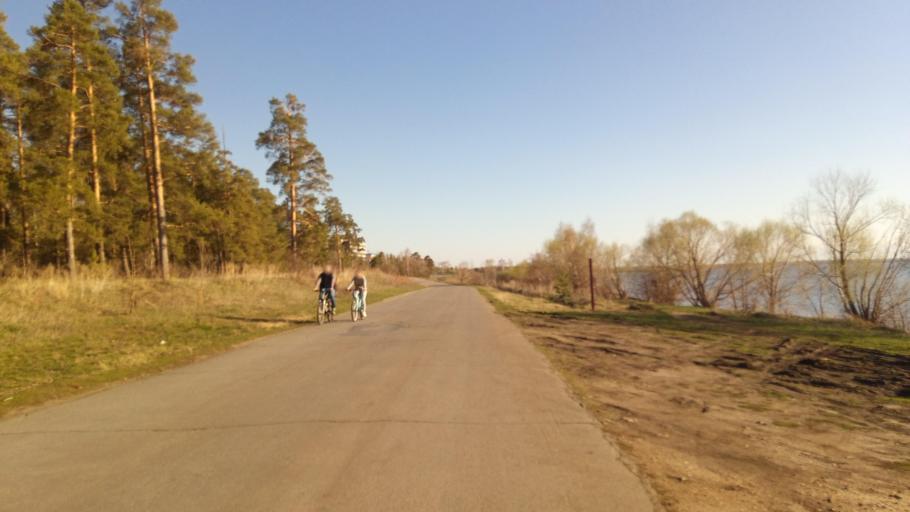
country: RU
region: Chelyabinsk
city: Novosineglazovskiy
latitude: 55.1289
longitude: 61.3281
